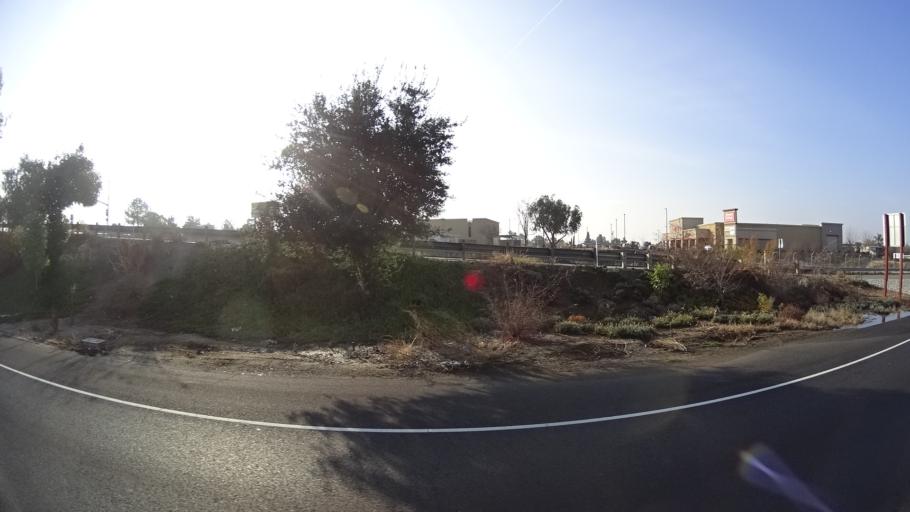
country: US
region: California
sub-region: Kern County
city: Bakersfield
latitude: 35.3941
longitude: -118.9686
